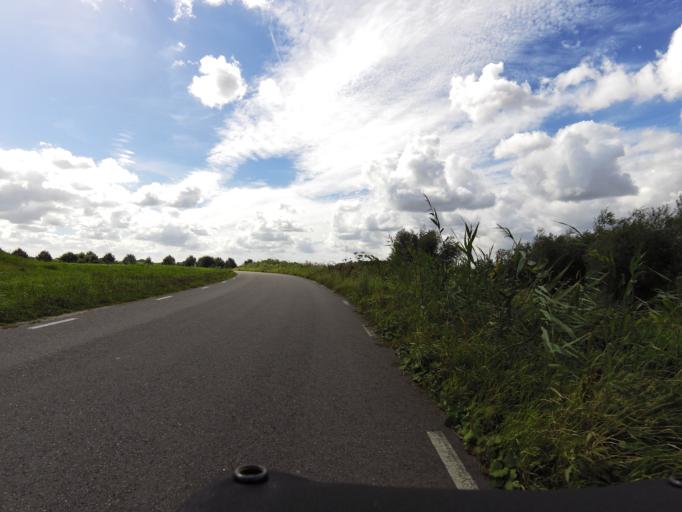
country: NL
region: South Holland
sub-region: Gemeente Oud-Beijerland
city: Oud-Beijerland
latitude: 51.8396
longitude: 4.3762
